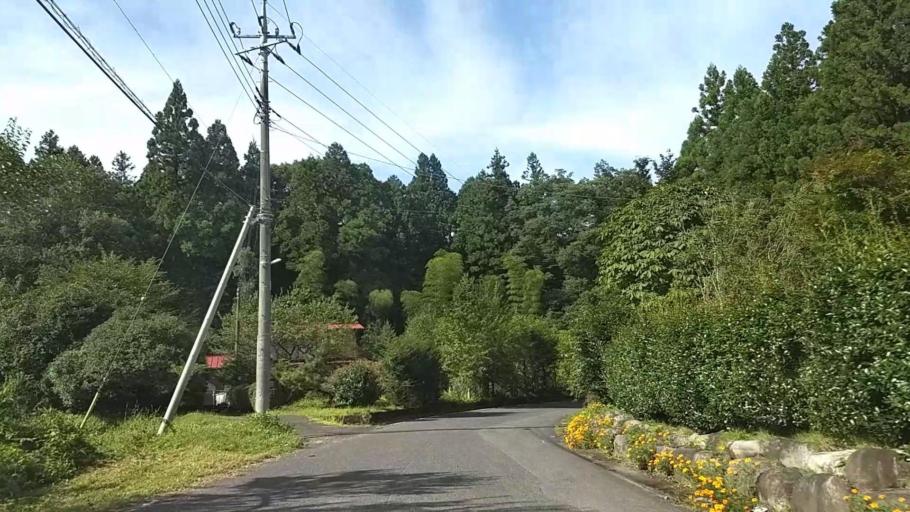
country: JP
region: Tochigi
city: Imaichi
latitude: 36.7879
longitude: 139.6960
